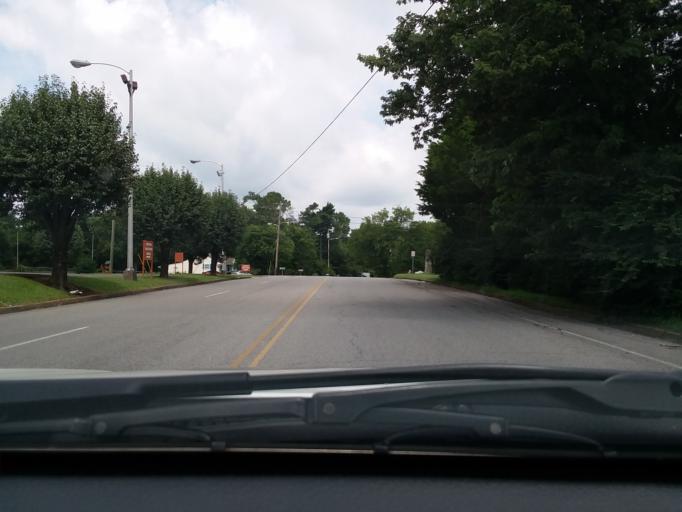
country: US
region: Tennessee
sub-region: Davidson County
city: Goodlettsville
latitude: 36.2961
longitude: -86.7047
